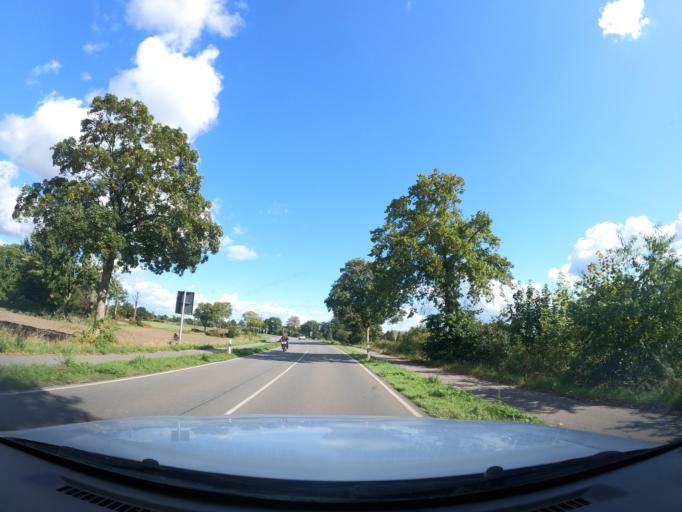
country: DE
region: North Rhine-Westphalia
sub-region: Regierungsbezirk Dusseldorf
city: Hunxe
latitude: 51.6456
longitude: 6.7812
